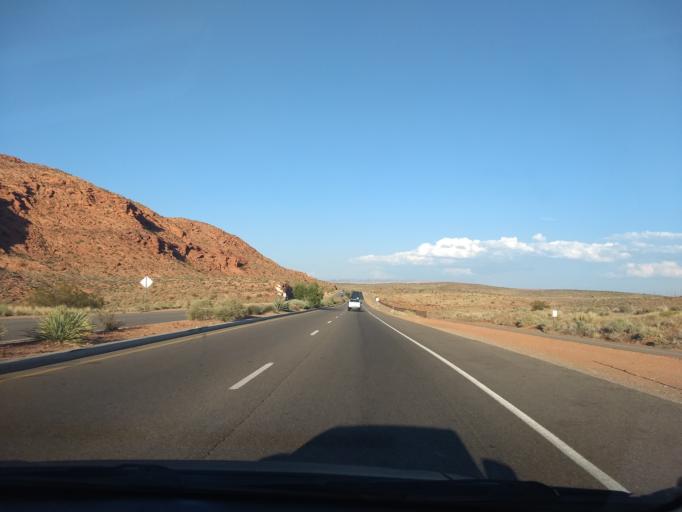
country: US
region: Utah
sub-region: Washington County
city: Saint George
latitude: 37.1345
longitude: -113.5963
